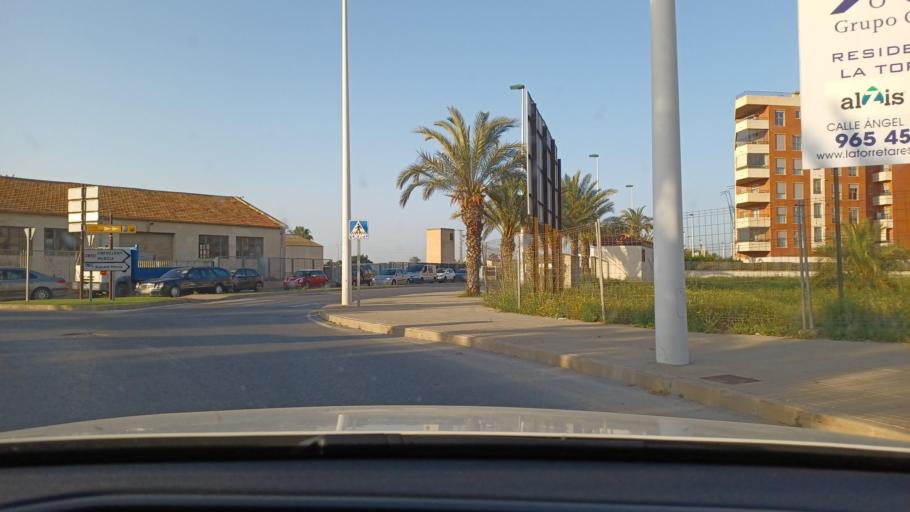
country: ES
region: Valencia
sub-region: Provincia de Alicante
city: Elche
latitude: 38.2531
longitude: -0.6941
